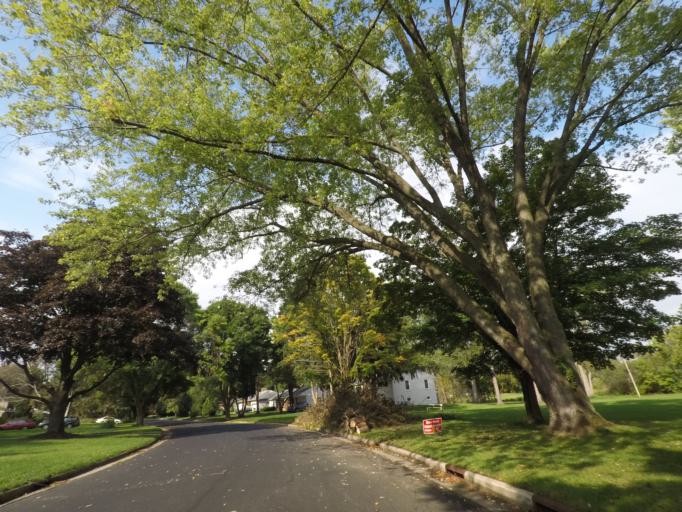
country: US
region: Wisconsin
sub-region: Dane County
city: Shorewood Hills
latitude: 43.0432
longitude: -89.4692
